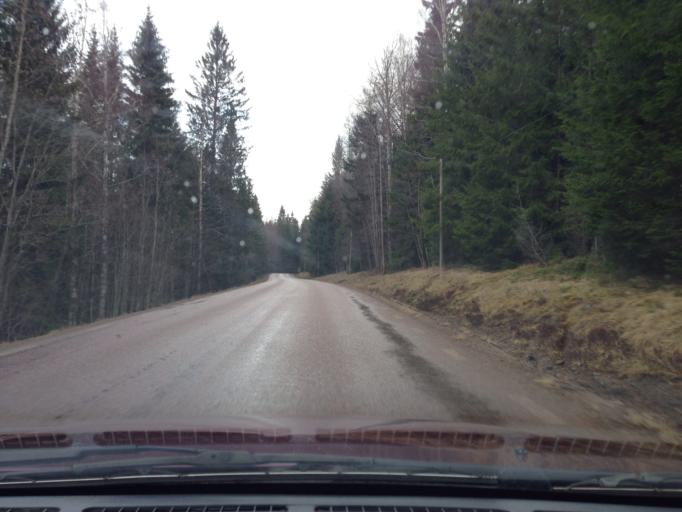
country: SE
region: Dalarna
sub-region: Ludvika Kommun
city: Ludvika
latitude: 60.1664
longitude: 15.2557
